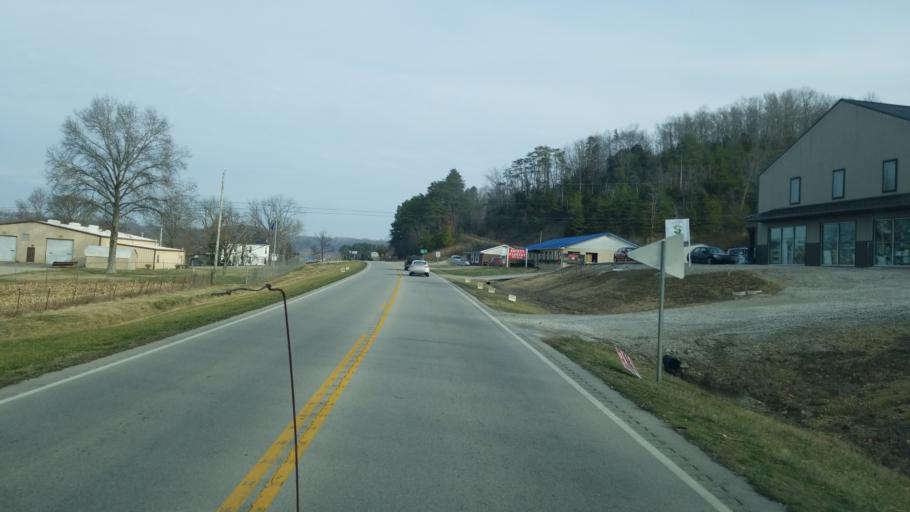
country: US
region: Kentucky
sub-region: Casey County
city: Liberty
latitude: 37.3027
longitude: -84.9464
